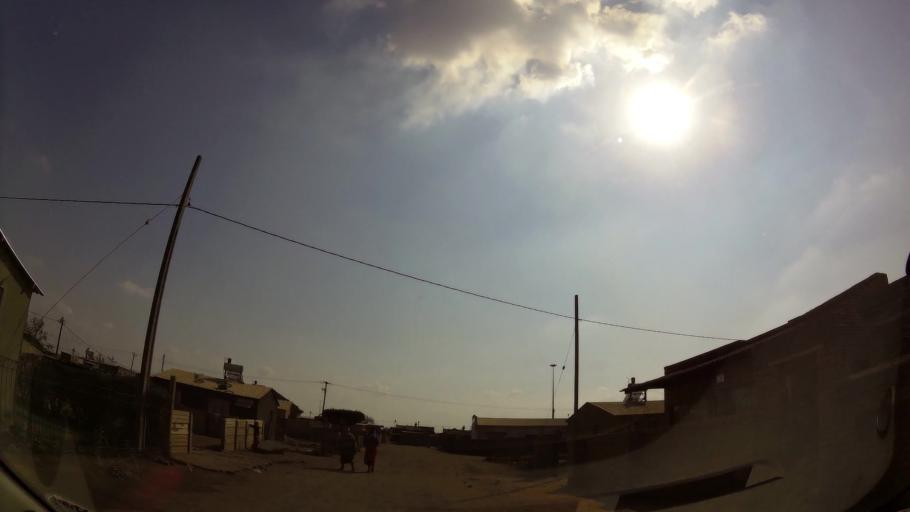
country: ZA
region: Gauteng
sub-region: Ekurhuleni Metropolitan Municipality
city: Springs
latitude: -26.1100
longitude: 28.4828
